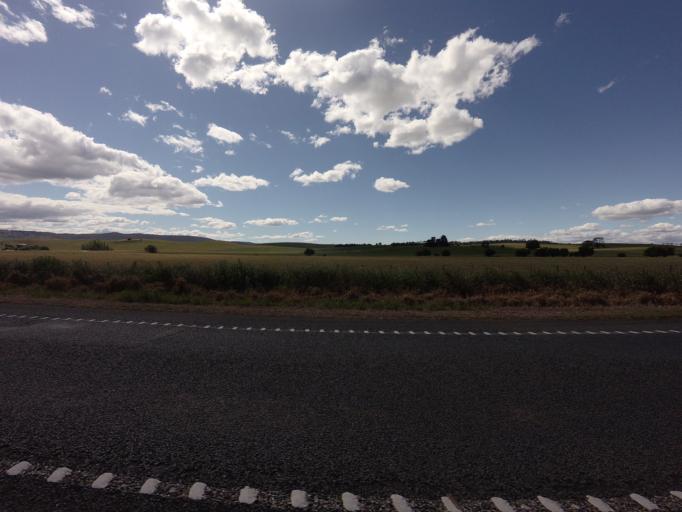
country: AU
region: Tasmania
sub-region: Northern Midlands
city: Evandale
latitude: -42.0156
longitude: 147.4885
